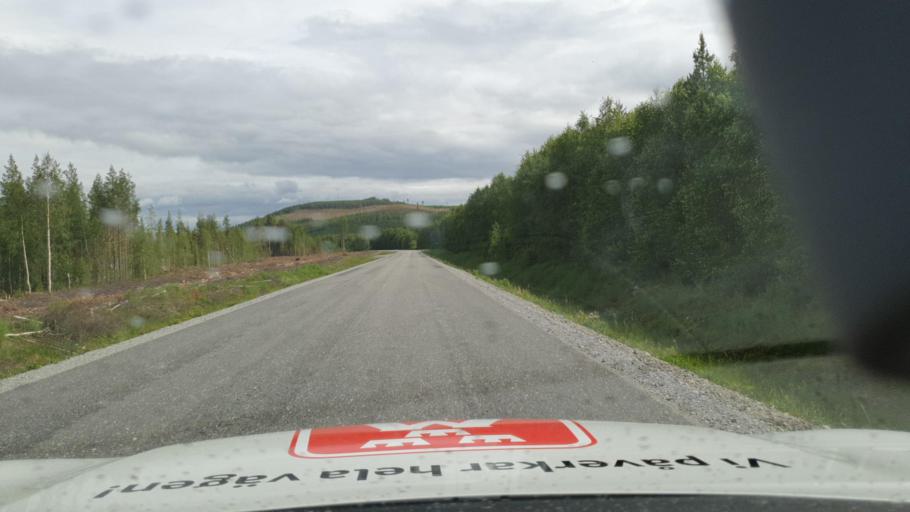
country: SE
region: Vaesterbotten
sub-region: Asele Kommun
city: Asele
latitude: 64.2073
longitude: 16.9386
